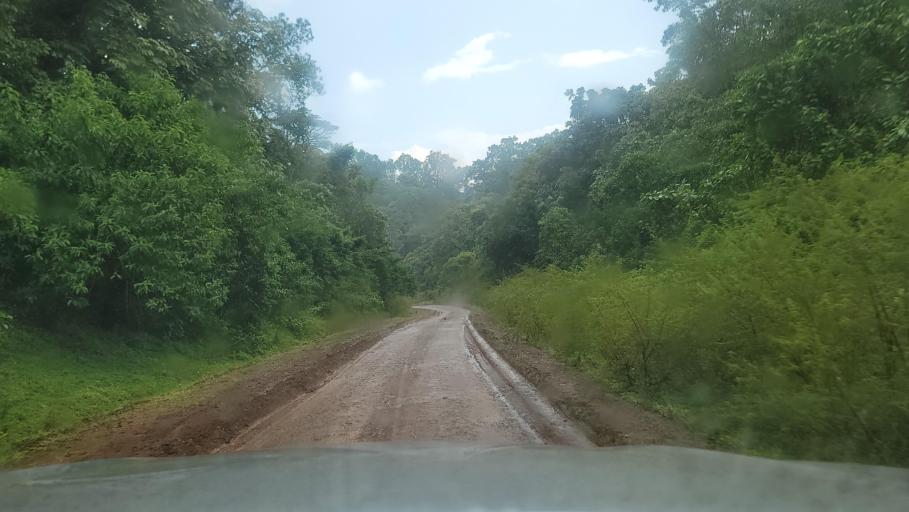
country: ET
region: Southern Nations, Nationalities, and People's Region
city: Bonga
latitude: 7.6723
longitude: 36.2429
